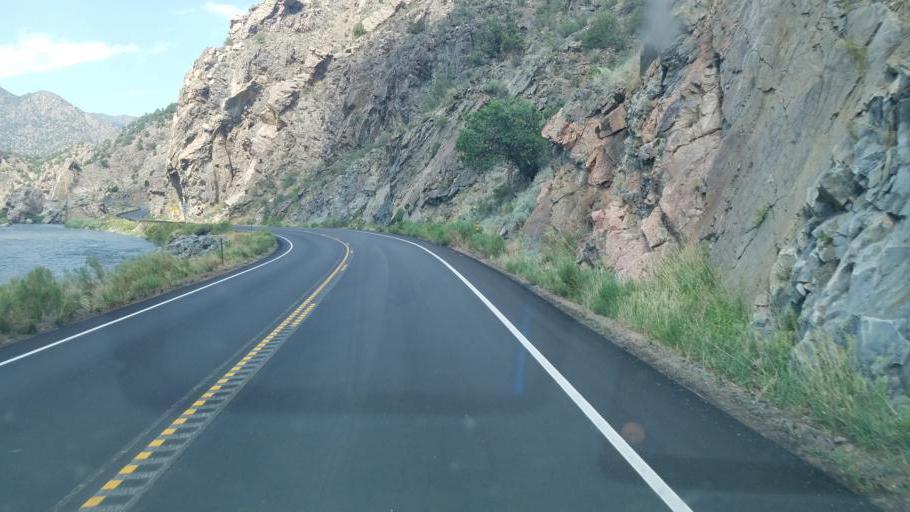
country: US
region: Colorado
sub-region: Fremont County
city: Canon City
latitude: 38.4299
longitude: -105.5431
